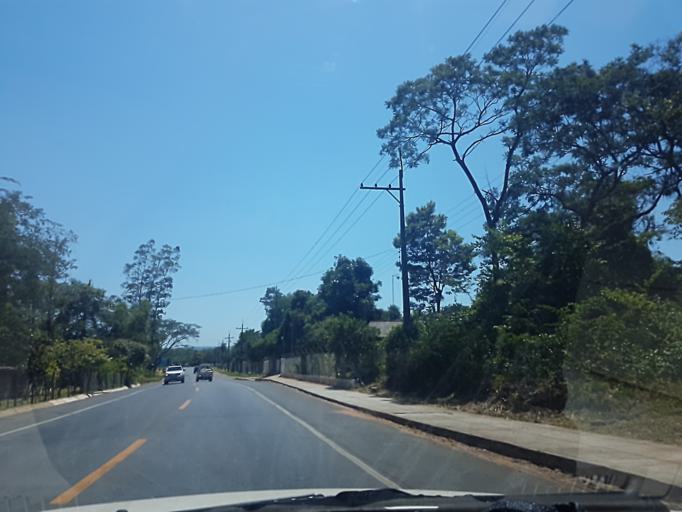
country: PY
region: Central
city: Aregua
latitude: -25.2391
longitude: -57.4258
